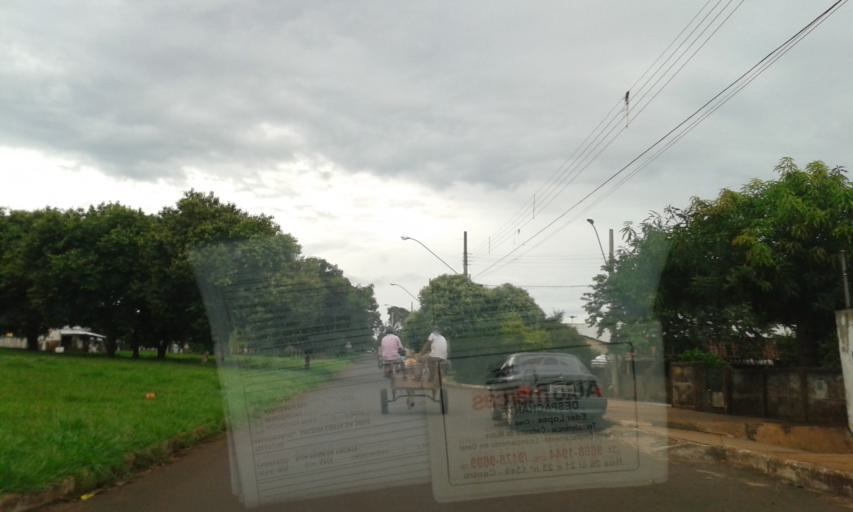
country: BR
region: Minas Gerais
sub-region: Ituiutaba
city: Ituiutaba
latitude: -18.9800
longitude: -49.4504
